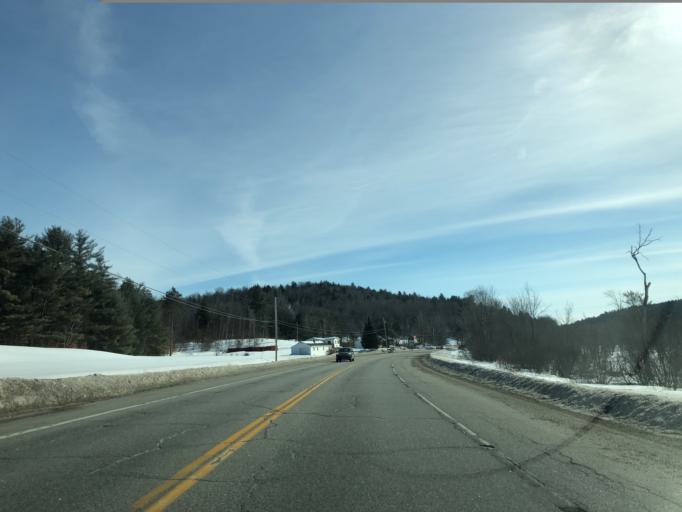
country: US
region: Maine
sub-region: Oxford County
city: West Paris
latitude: 44.3234
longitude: -70.5470
